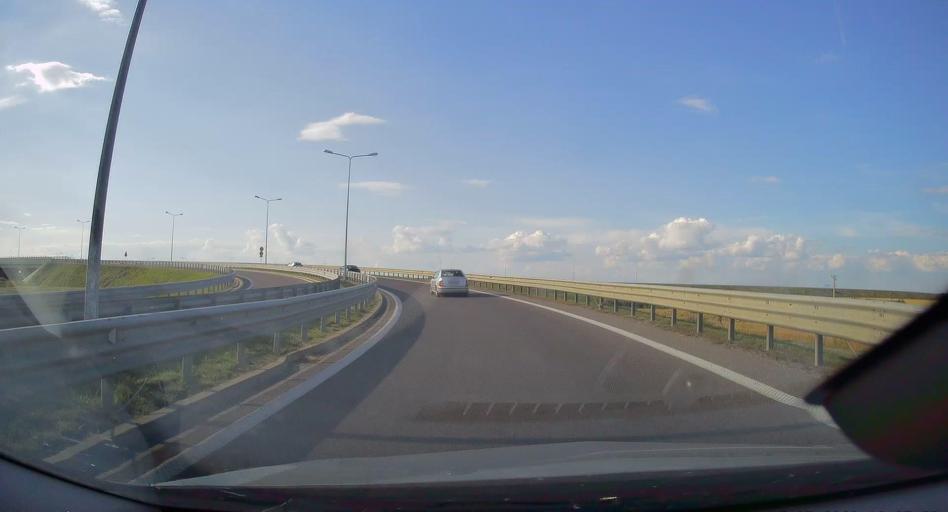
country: PL
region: Subcarpathian Voivodeship
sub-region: Powiat przemyski
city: Orly
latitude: 49.9069
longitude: 22.8199
